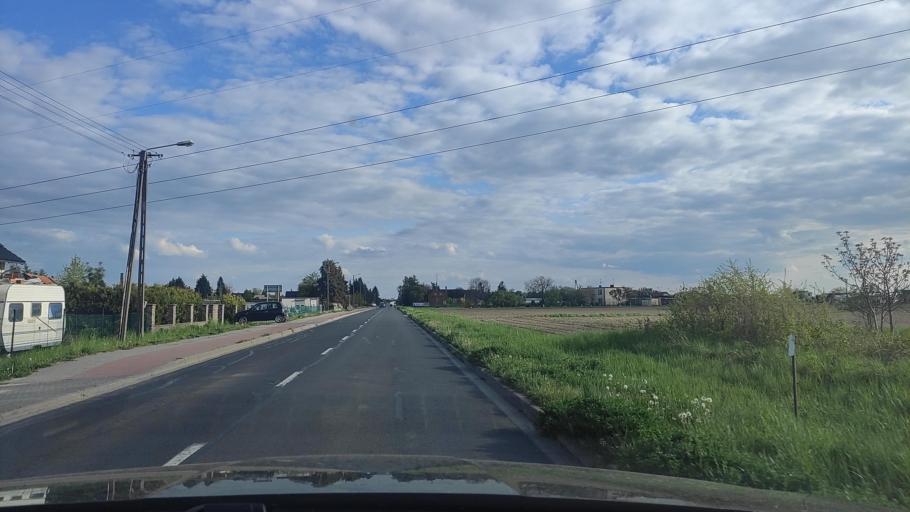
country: PL
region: Greater Poland Voivodeship
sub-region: Powiat poznanski
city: Kostrzyn
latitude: 52.4090
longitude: 17.2252
